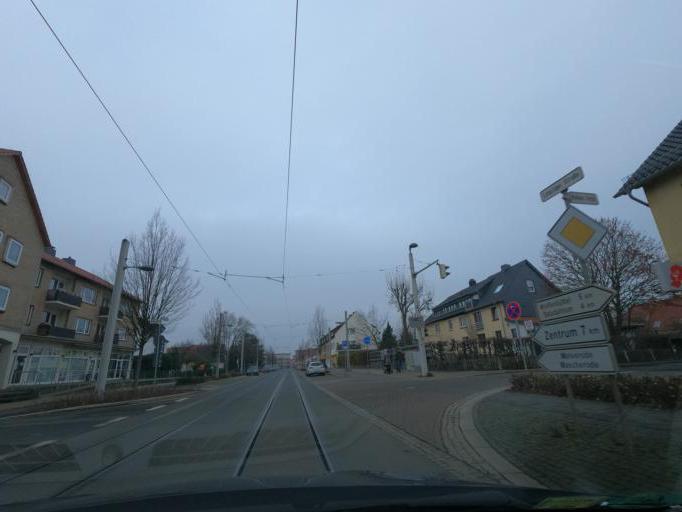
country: DE
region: Lower Saxony
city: Leiferde
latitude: 52.2109
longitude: 10.5235
